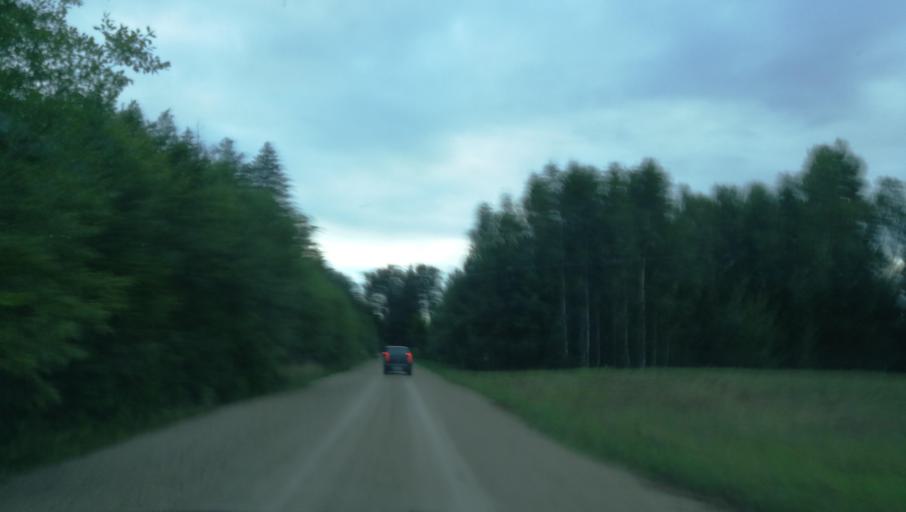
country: LV
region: Incukalns
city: Incukalns
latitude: 57.0298
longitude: 24.7905
